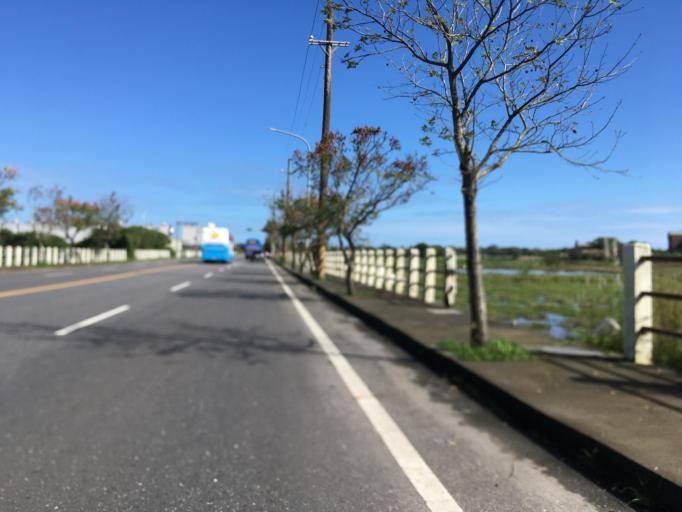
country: TW
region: Taiwan
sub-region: Yilan
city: Yilan
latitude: 24.6144
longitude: 121.8435
